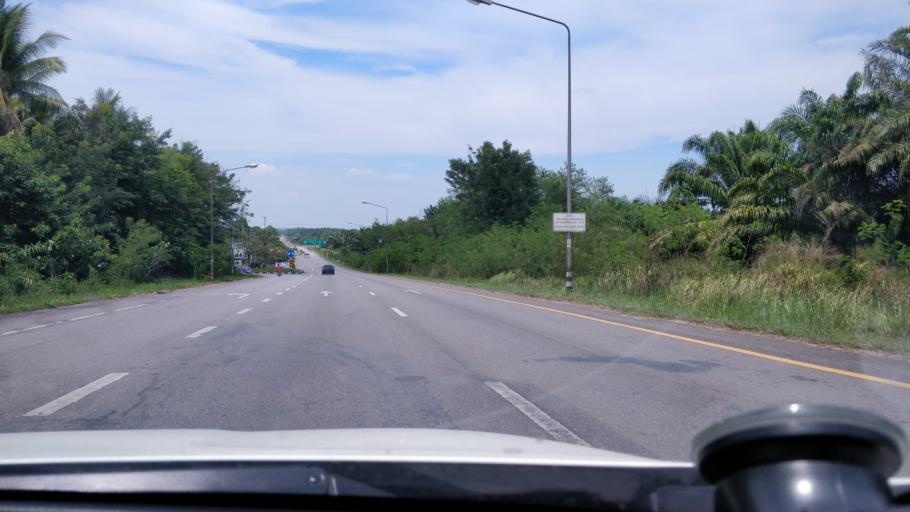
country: TH
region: Krabi
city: Plai Phraya
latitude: 8.6167
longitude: 98.9954
